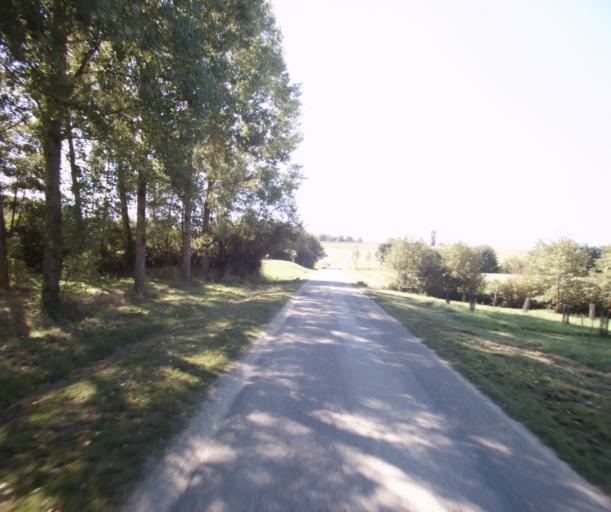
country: FR
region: Midi-Pyrenees
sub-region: Departement du Gers
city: Cazaubon
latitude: 43.9308
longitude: -0.0232
